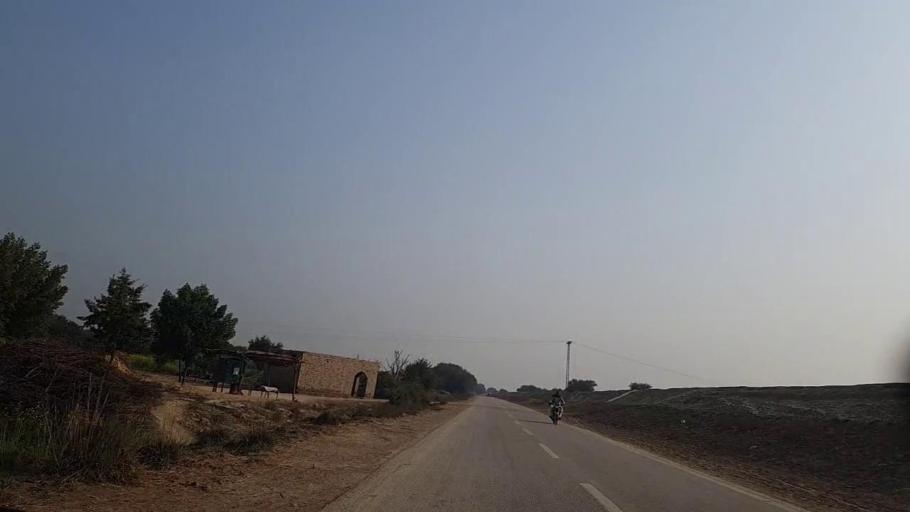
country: PK
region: Sindh
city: Sann
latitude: 26.1630
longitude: 68.1129
